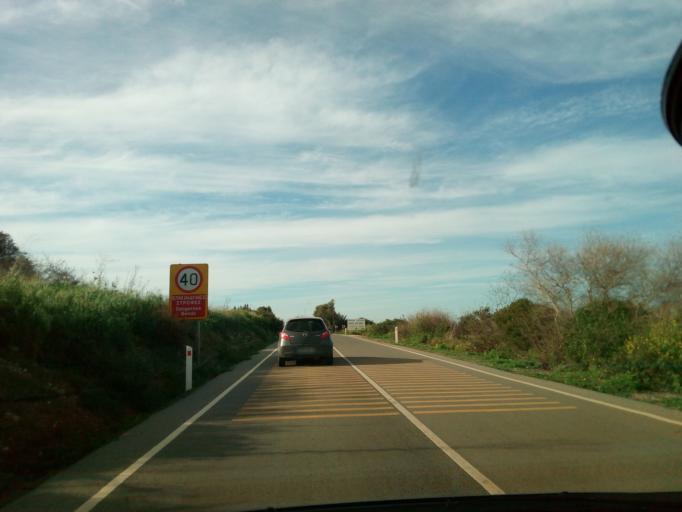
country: CY
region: Pafos
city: Polis
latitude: 35.0497
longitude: 32.3535
